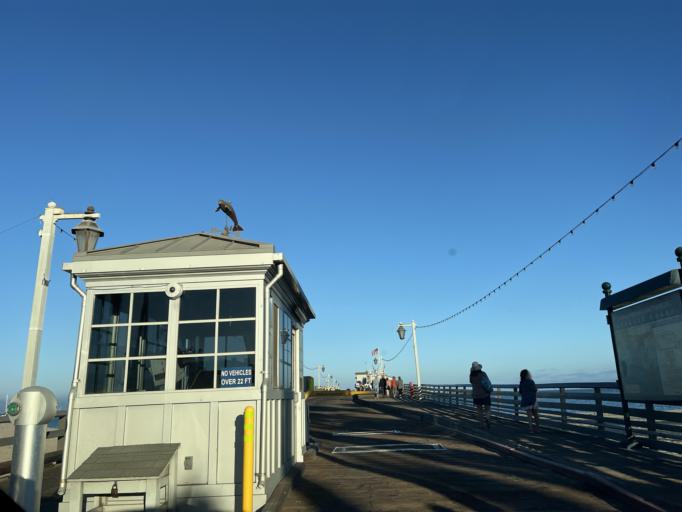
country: US
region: California
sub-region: Santa Barbara County
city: Santa Barbara
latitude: 34.4119
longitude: -119.6888
